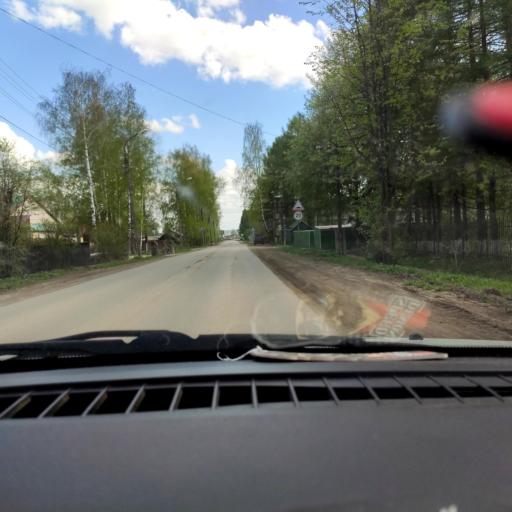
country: RU
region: Perm
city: Kudymkar
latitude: 59.0178
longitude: 54.6498
